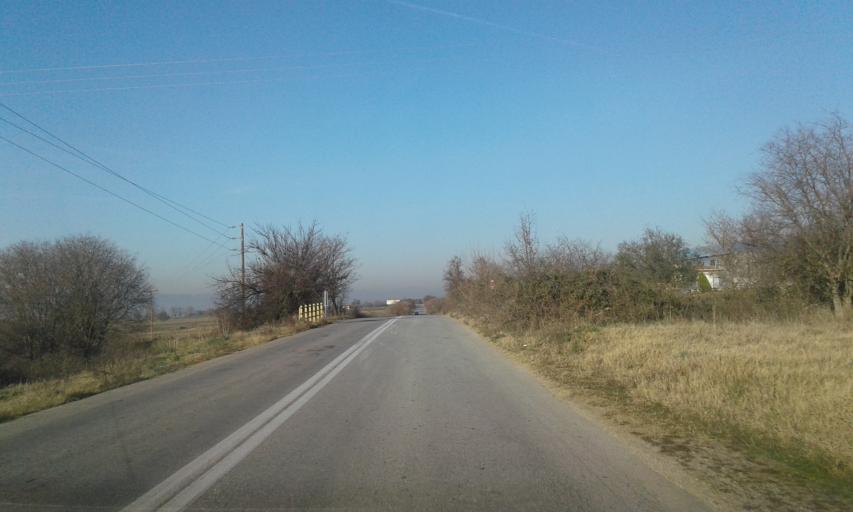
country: GR
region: Central Macedonia
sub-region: Nomos Thessalonikis
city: Gerakarou
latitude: 40.6891
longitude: 23.2292
